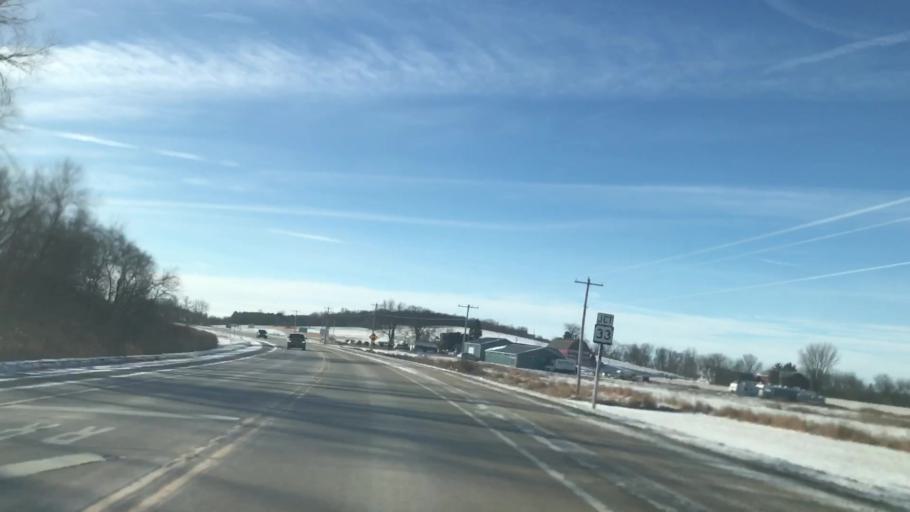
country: US
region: Wisconsin
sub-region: Dodge County
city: Mayville
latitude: 43.4457
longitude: -88.5443
